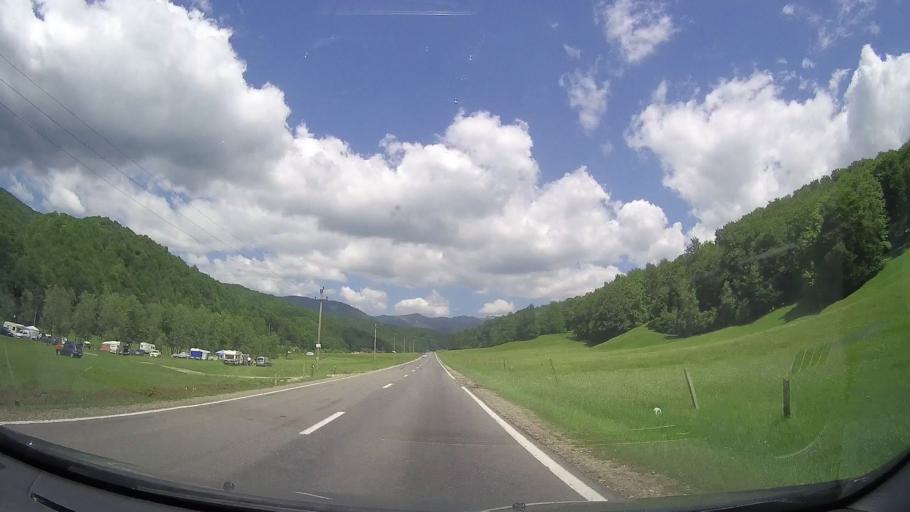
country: RO
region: Prahova
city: Maneciu
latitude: 45.4248
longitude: 25.9413
